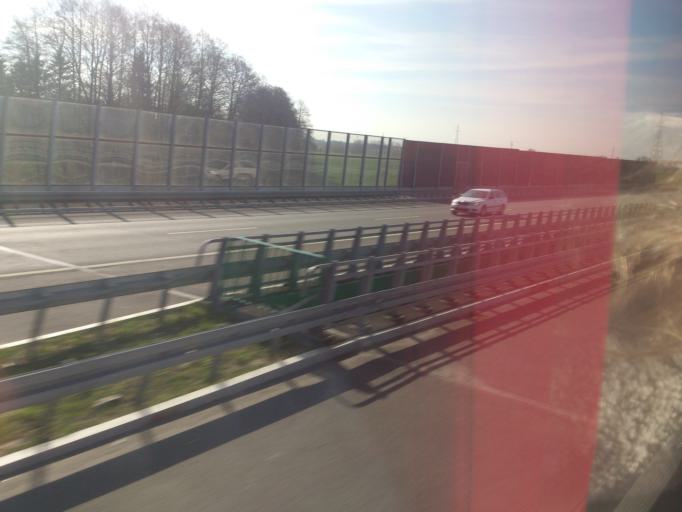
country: PL
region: Kujawsko-Pomorskie
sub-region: Powiat wloclawski
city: Lubanie
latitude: 52.7411
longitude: 18.8585
